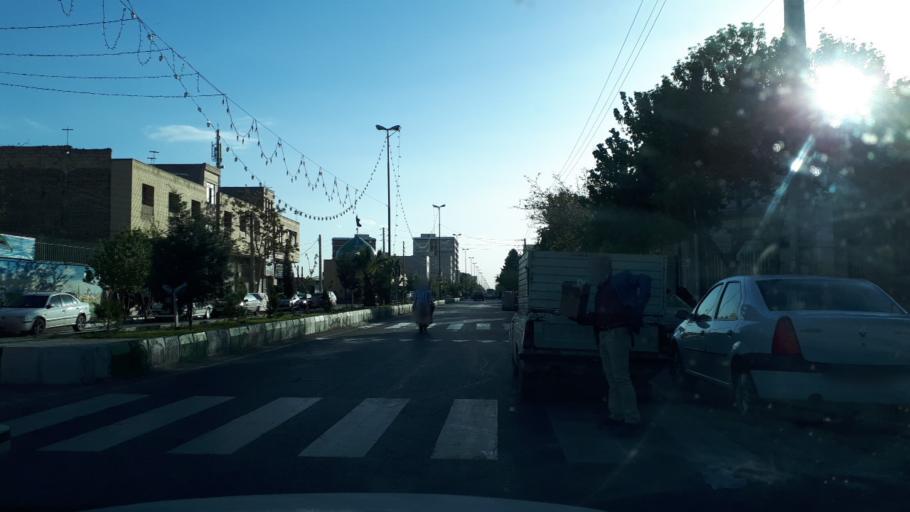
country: IR
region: Semnan
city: Semnan
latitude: 35.5650
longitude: 53.3943
